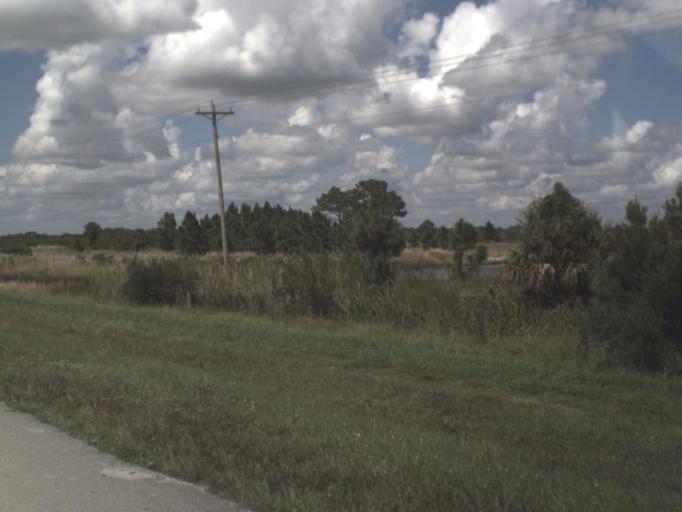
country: US
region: Florida
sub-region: Lee County
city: Lehigh Acres
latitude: 26.5169
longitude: -81.5577
